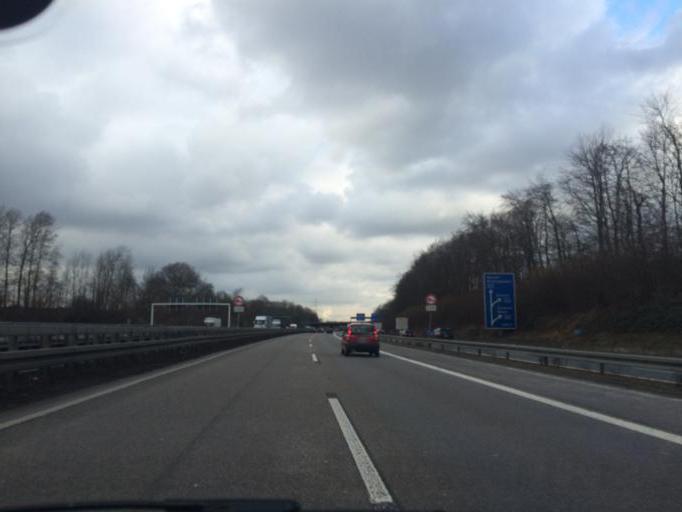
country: DE
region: North Rhine-Westphalia
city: Witten
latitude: 51.4563
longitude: 7.2890
